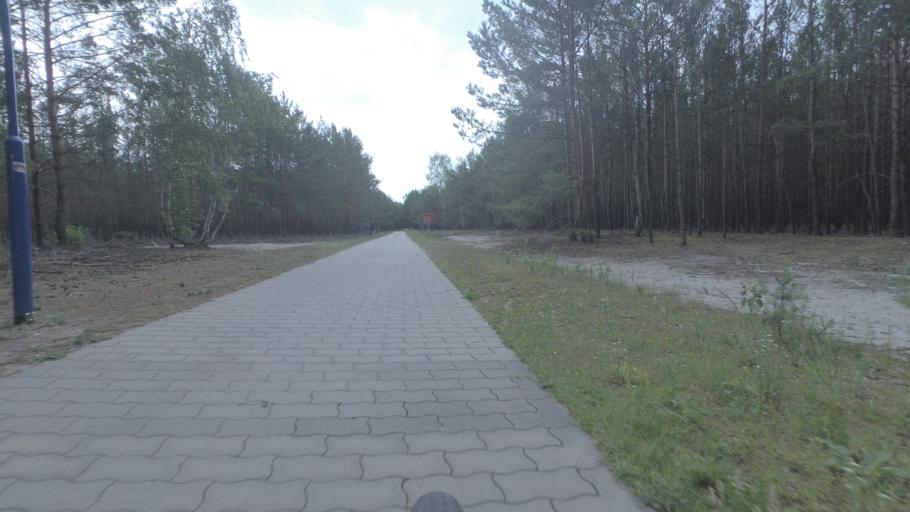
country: DE
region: Brandenburg
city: Bestensee
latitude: 52.2404
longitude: 13.6558
